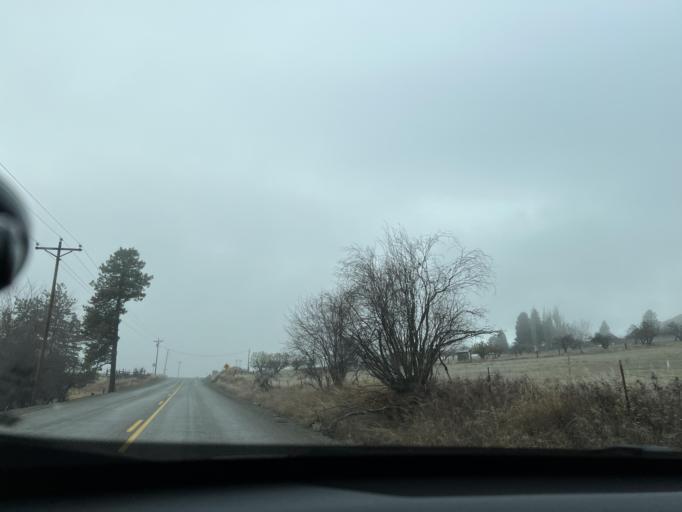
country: US
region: Washington
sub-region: Okanogan County
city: Brewster
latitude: 48.4481
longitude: -120.2020
